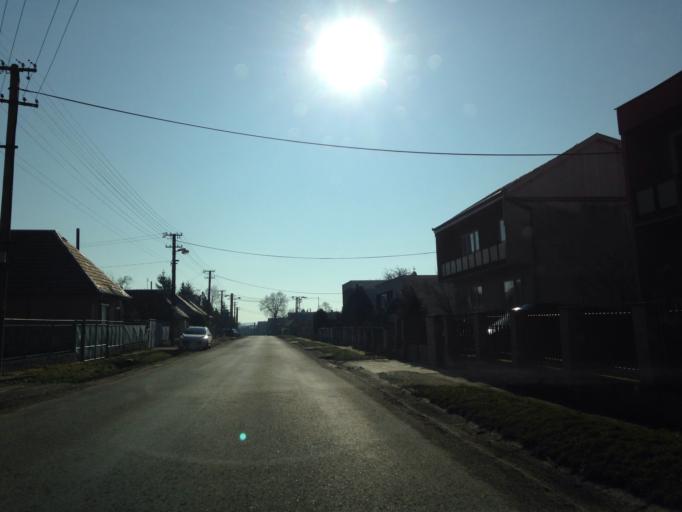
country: SK
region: Nitriansky
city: Svodin
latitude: 47.9074
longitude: 18.4119
